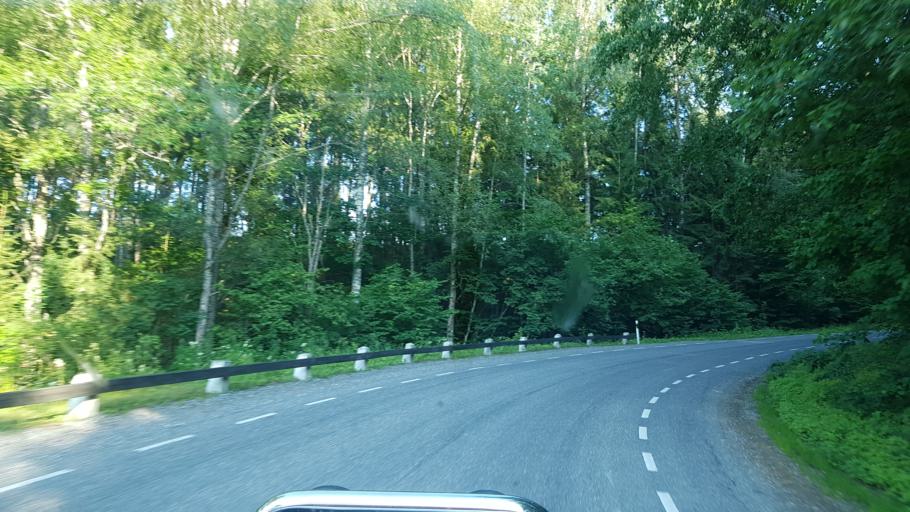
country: EE
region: Polvamaa
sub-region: Polva linn
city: Polva
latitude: 58.0147
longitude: 26.9215
